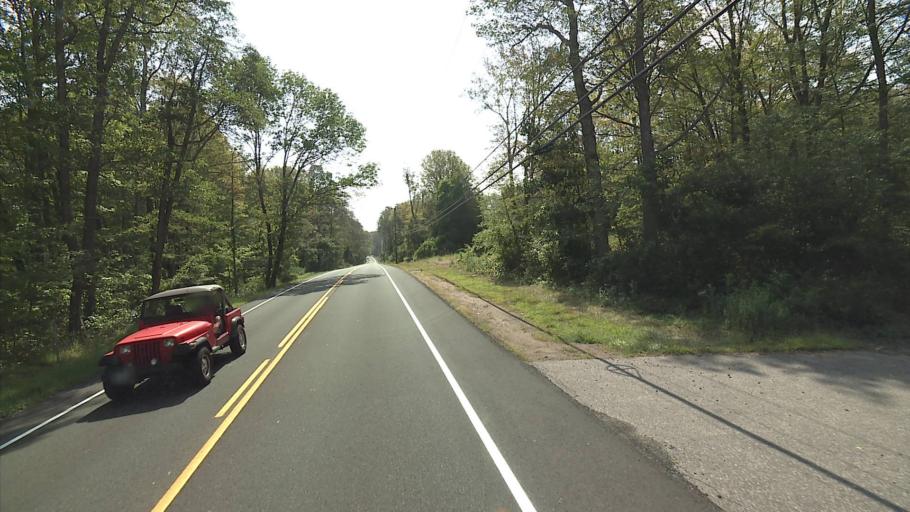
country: US
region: Connecticut
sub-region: Middlesex County
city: Durham
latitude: 41.3900
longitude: -72.6481
